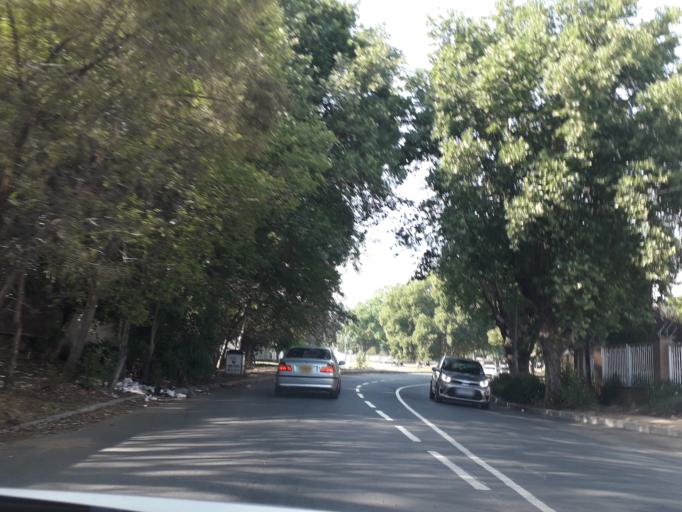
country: ZA
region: Gauteng
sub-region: City of Johannesburg Metropolitan Municipality
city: Johannesburg
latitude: -26.1615
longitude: 28.0584
